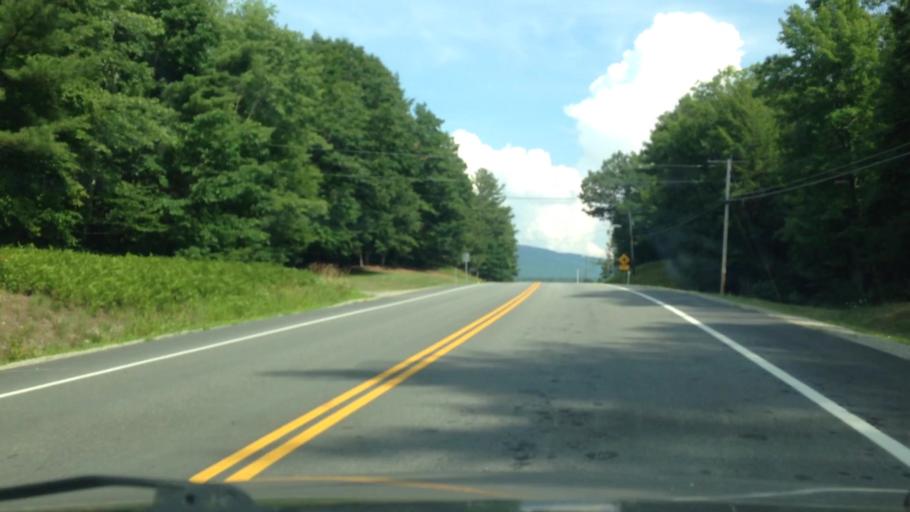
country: US
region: New Hampshire
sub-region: Cheshire County
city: Marlborough
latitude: 42.8801
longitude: -72.1919
